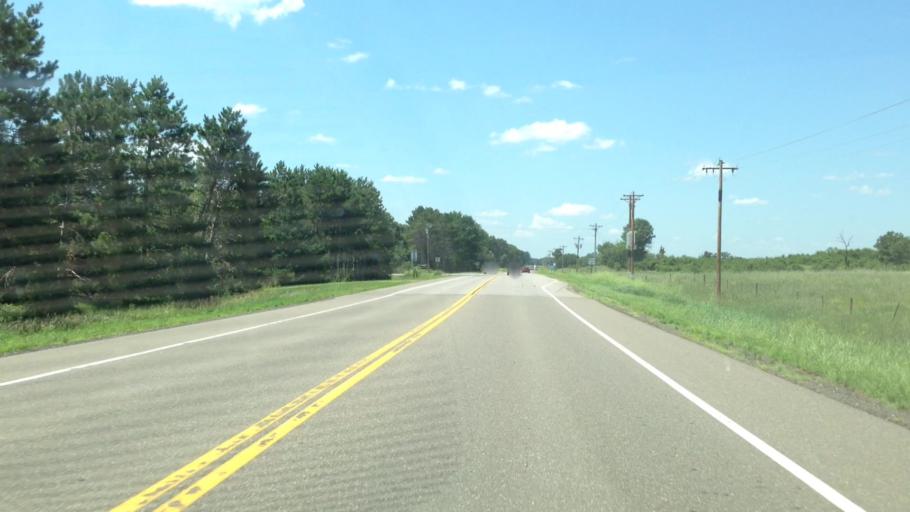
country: US
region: Minnesota
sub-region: Sherburne County
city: Zimmerman
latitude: 45.4439
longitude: -93.6768
